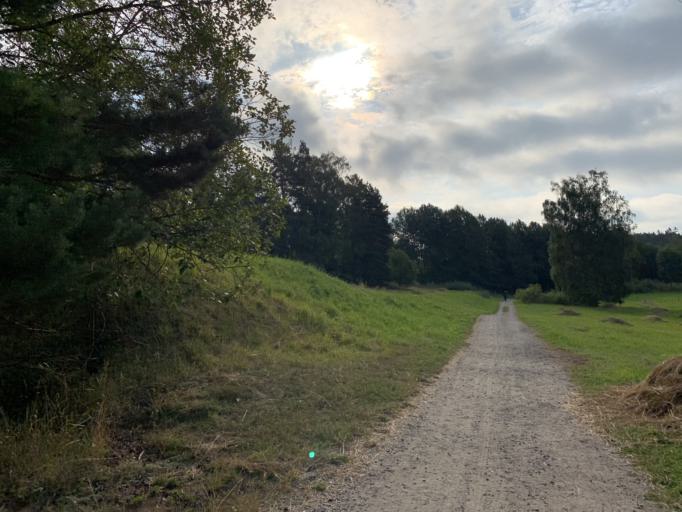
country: SE
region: Stockholm
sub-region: Solna Kommun
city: Rasunda
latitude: 59.3928
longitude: 17.9846
